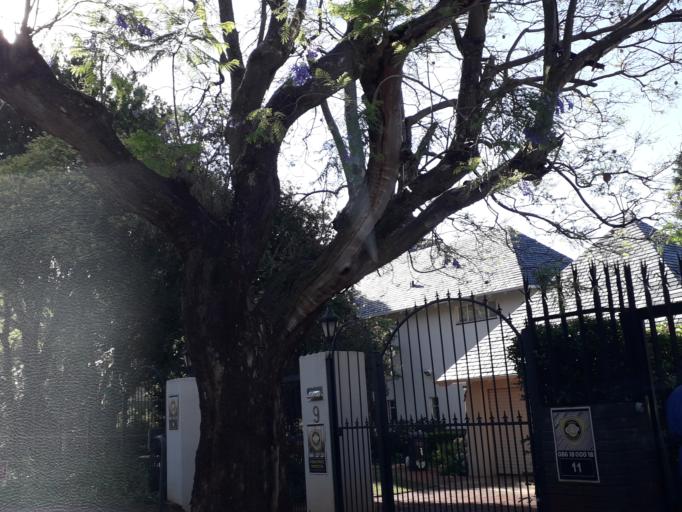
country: ZA
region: Gauteng
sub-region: City of Johannesburg Metropolitan Municipality
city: Johannesburg
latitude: -26.1622
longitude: 28.0075
